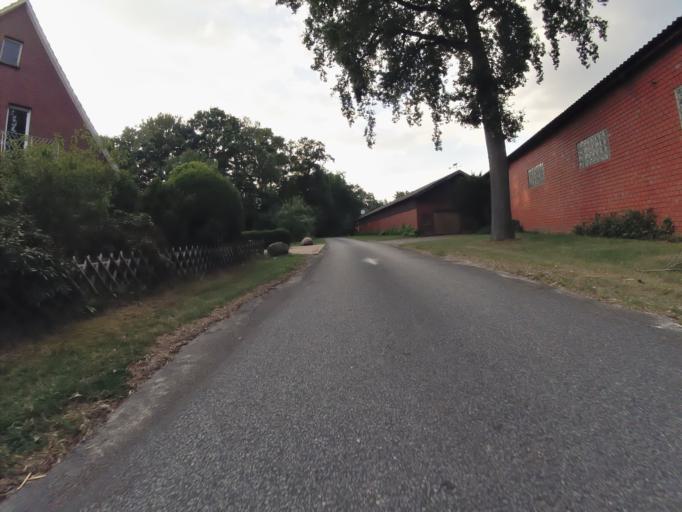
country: DE
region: North Rhine-Westphalia
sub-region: Regierungsbezirk Munster
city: Westerkappeln
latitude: 52.3396
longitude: 7.8881
